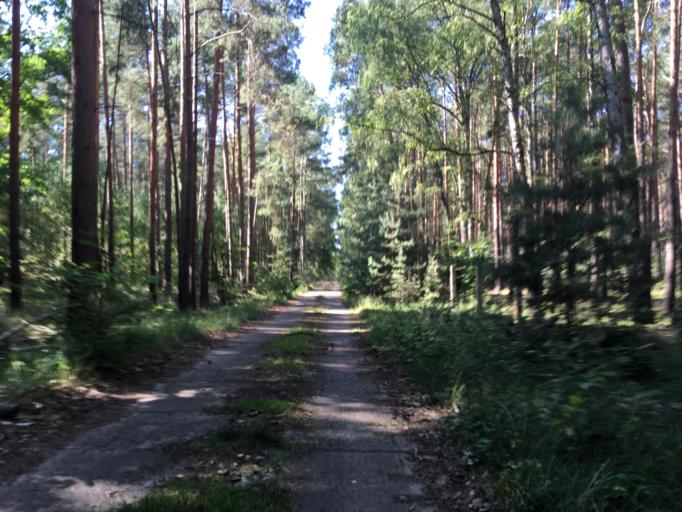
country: DE
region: Brandenburg
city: Gross Koris
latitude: 52.1943
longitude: 13.7260
